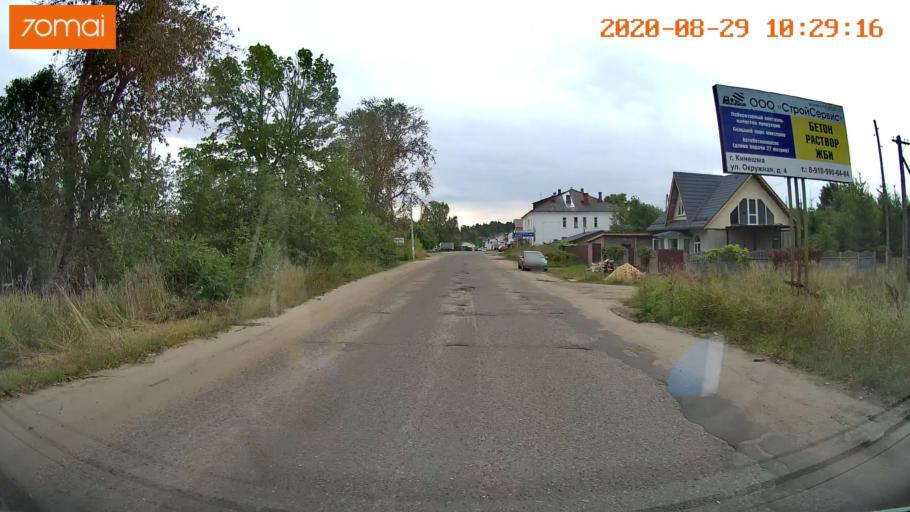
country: RU
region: Ivanovo
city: Yur'yevets
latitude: 57.3111
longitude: 43.0951
